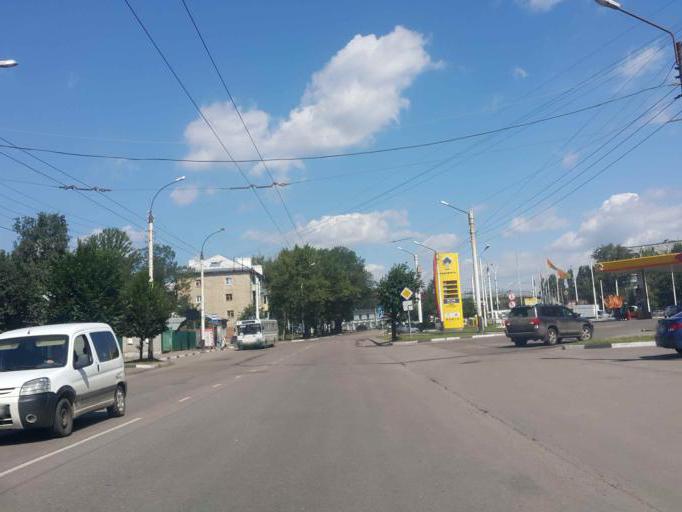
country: RU
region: Tambov
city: Tambov
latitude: 52.7349
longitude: 41.4415
